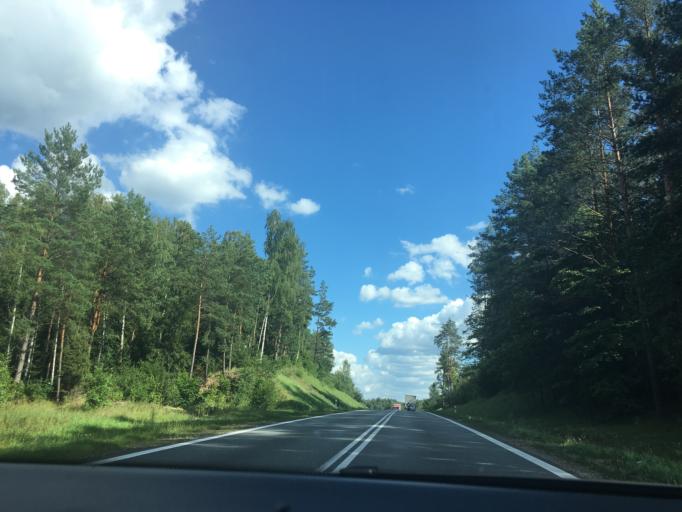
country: PL
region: Podlasie
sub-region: Powiat bialostocki
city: Wasilkow
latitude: 53.2698
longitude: 23.1216
